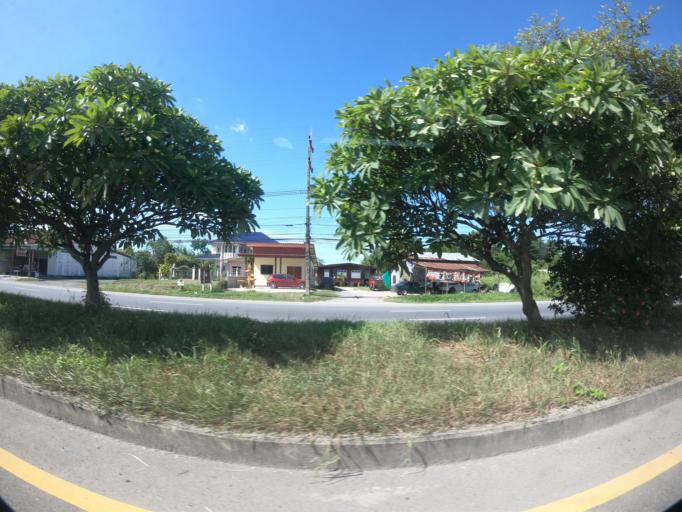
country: TH
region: Nakhon Nayok
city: Ban Na
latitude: 14.2559
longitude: 101.0835
